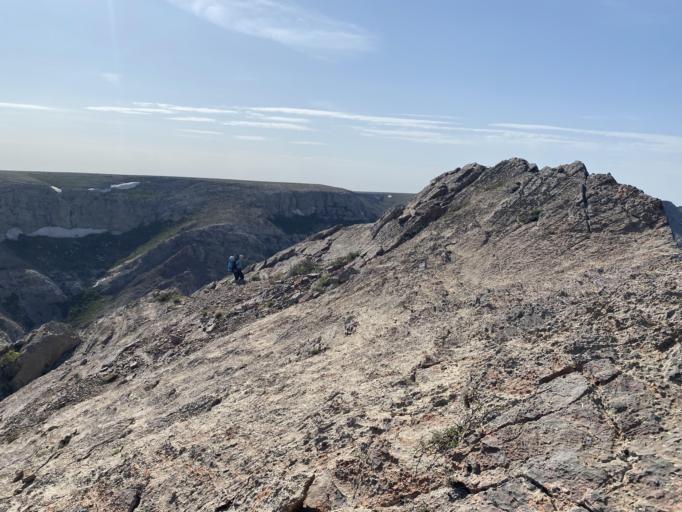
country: KZ
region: Ongtustik Qazaqstan
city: Kentau
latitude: 43.8600
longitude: 68.4174
